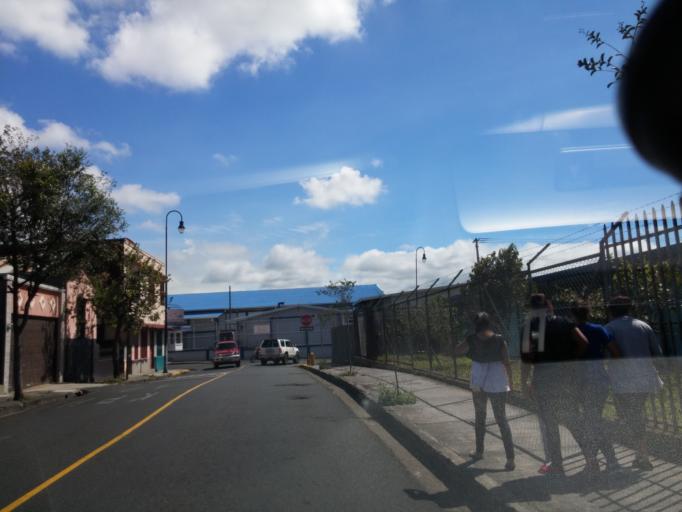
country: CR
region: San Jose
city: San Jose
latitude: 9.9263
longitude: -84.0875
